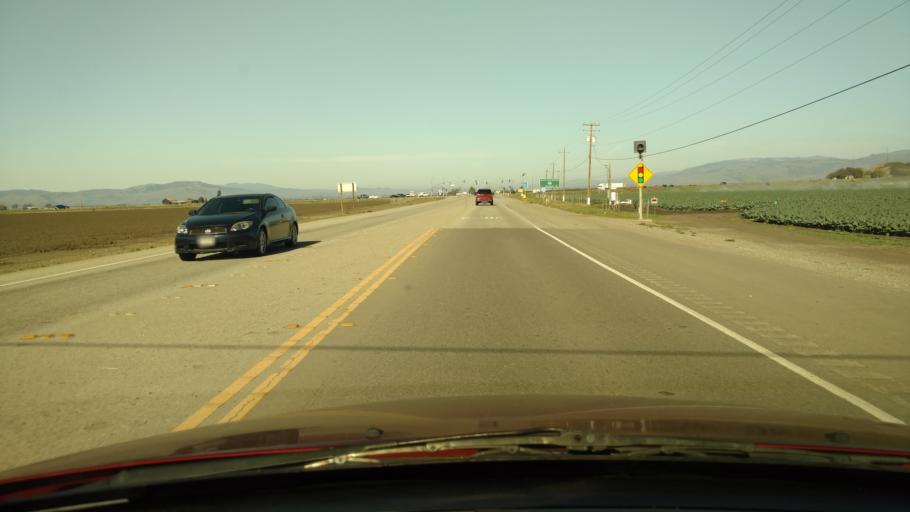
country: US
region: California
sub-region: San Benito County
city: Hollister
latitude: 36.8929
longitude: -121.4246
